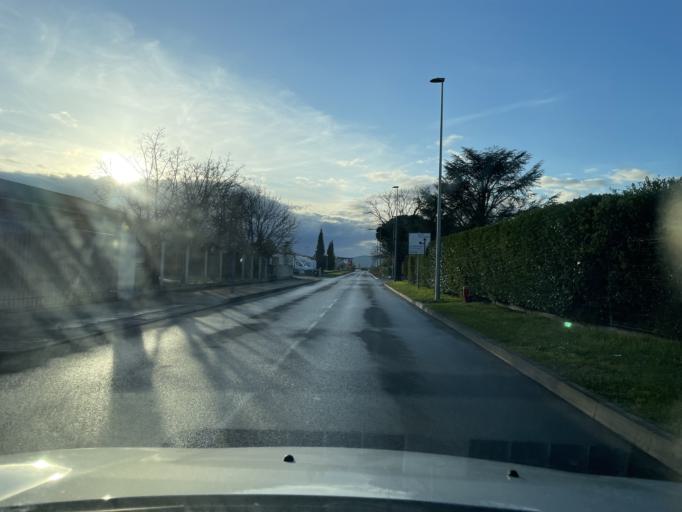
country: FR
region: Midi-Pyrenees
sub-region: Departement de la Haute-Garonne
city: Tournefeuille
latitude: 43.6007
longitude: 1.3068
